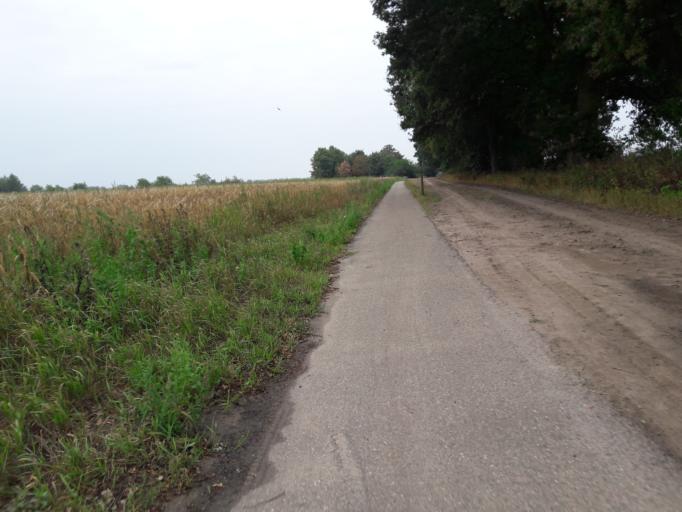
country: NL
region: Drenthe
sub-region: Gemeente Borger-Odoorn
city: Borger
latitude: 52.9411
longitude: 6.8224
